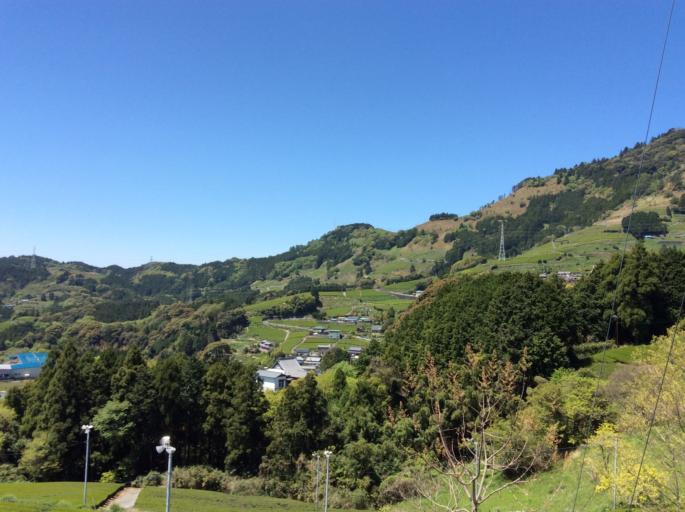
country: JP
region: Shizuoka
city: Kanaya
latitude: 34.8364
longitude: 138.0812
